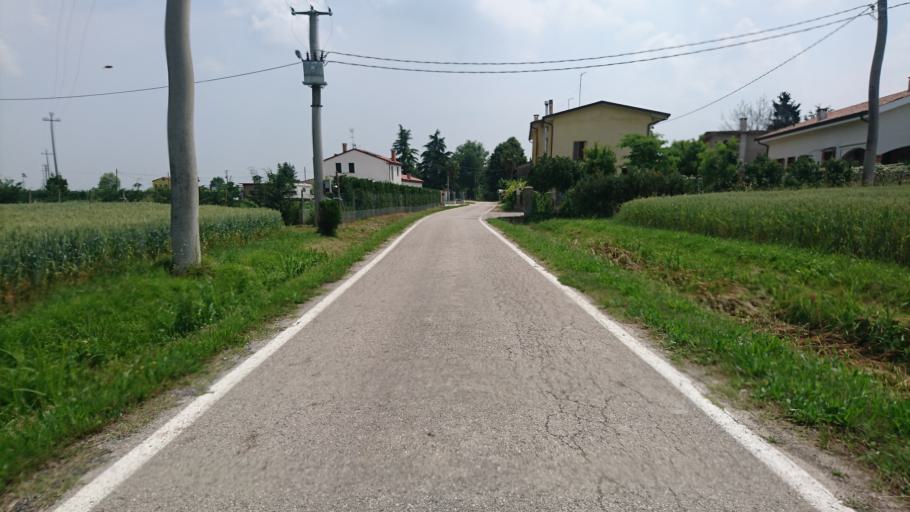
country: IT
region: Veneto
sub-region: Provincia di Padova
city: Cartura
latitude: 45.2697
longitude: 11.8696
